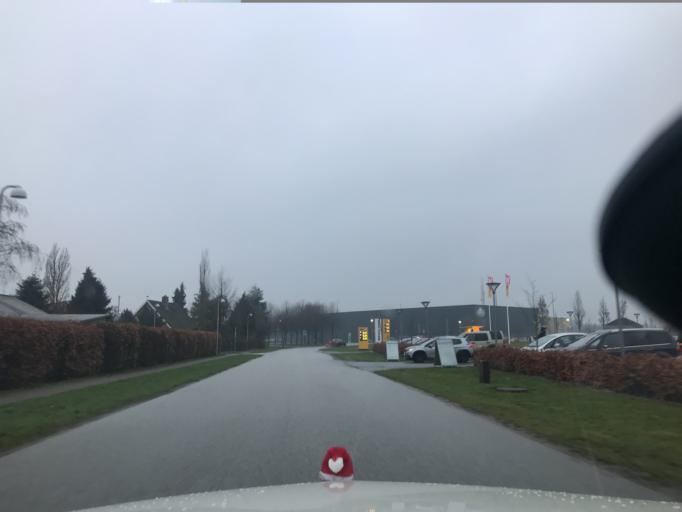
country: DK
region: South Denmark
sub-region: Aabenraa Kommune
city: Krusa
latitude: 54.8494
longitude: 9.4089
